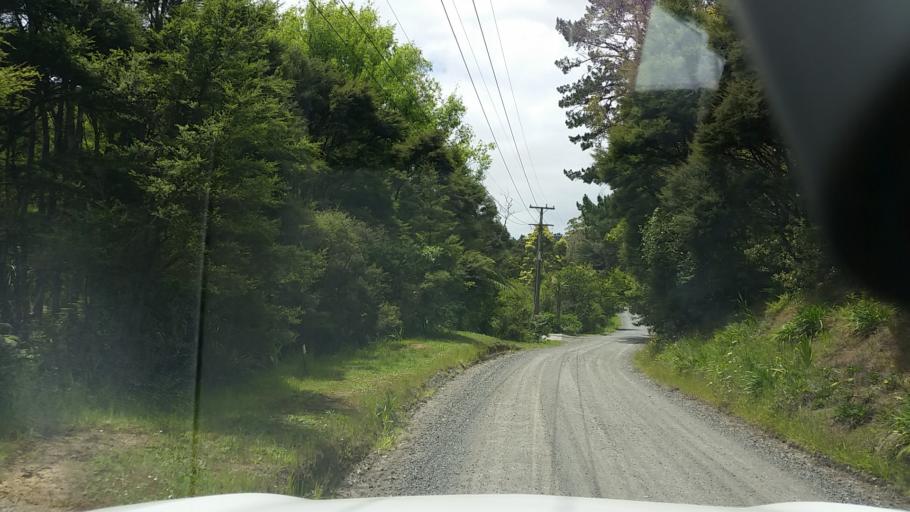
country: NZ
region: Auckland
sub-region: Auckland
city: Rosebank
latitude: -36.8527
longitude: 174.5894
